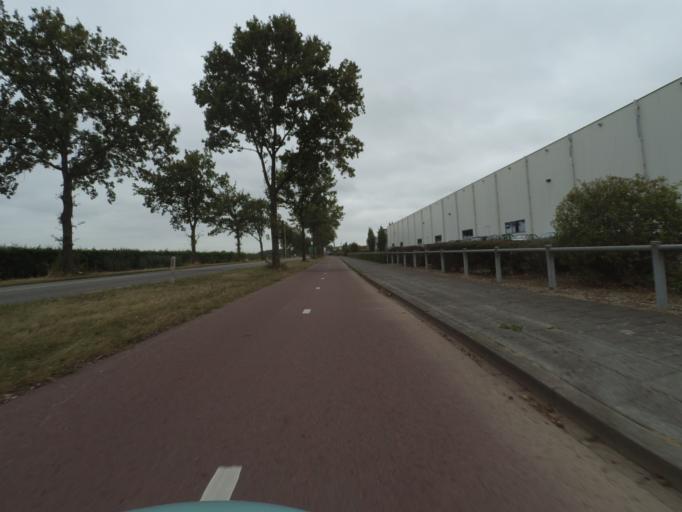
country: NL
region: Gelderland
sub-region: Gemeente Tiel
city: Tiel
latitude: 51.9105
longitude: 5.4261
